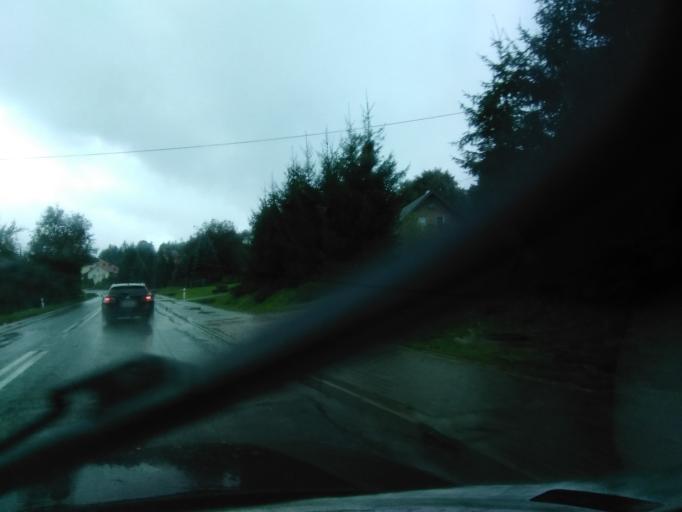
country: PL
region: Subcarpathian Voivodeship
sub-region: Powiat ropczycko-sedziszowski
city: Niedzwiada
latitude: 50.0165
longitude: 21.5500
